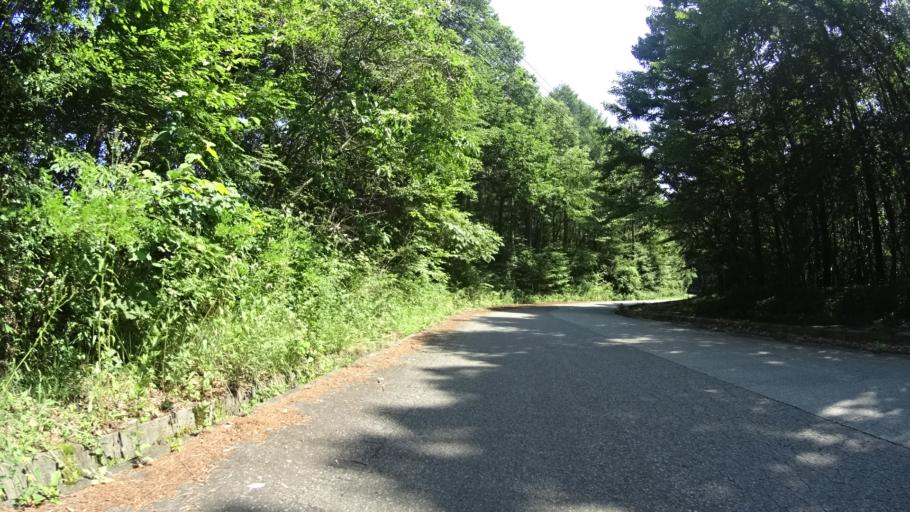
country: JP
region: Yamanashi
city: Nirasaki
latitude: 35.9108
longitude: 138.4291
